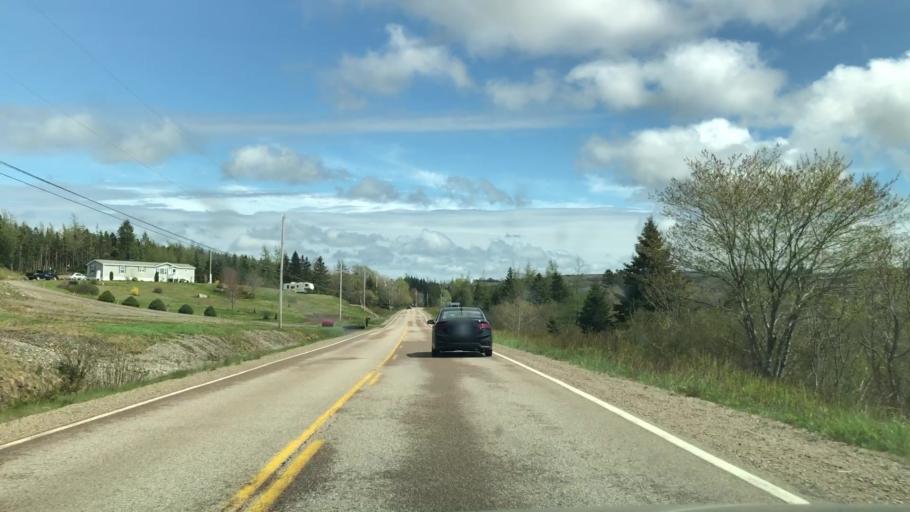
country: CA
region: Nova Scotia
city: Antigonish
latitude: 45.1883
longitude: -61.9878
